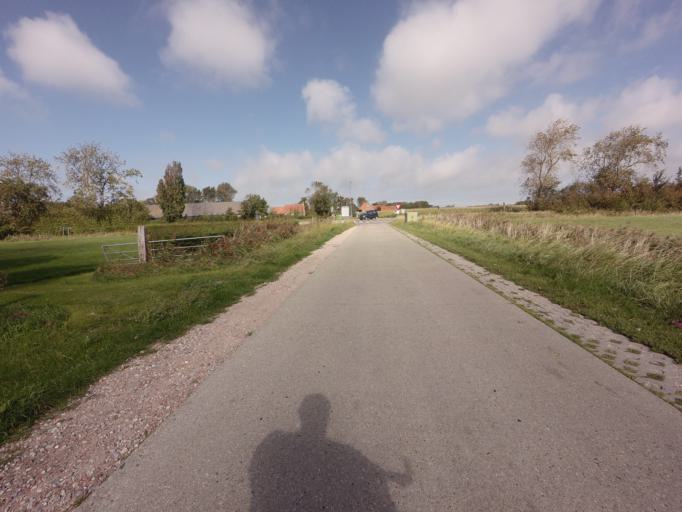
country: NL
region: Zeeland
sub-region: Gemeente Middelburg
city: Middelburg
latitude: 51.5461
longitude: 3.5181
